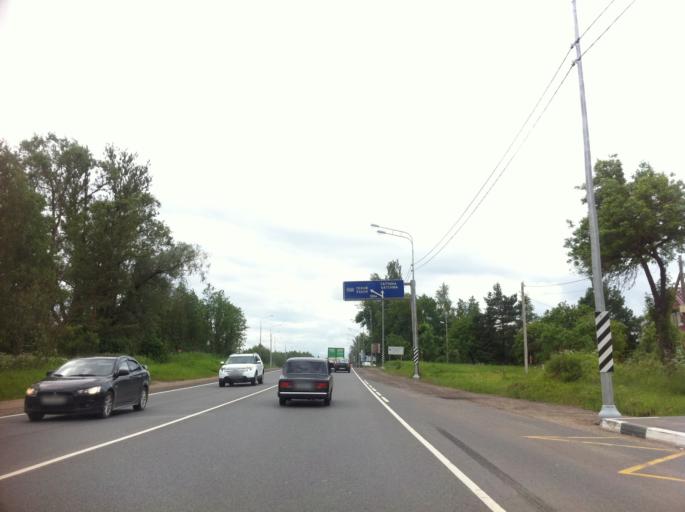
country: RU
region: Leningrad
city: Maloye Verevo
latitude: 59.6020
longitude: 30.1611
